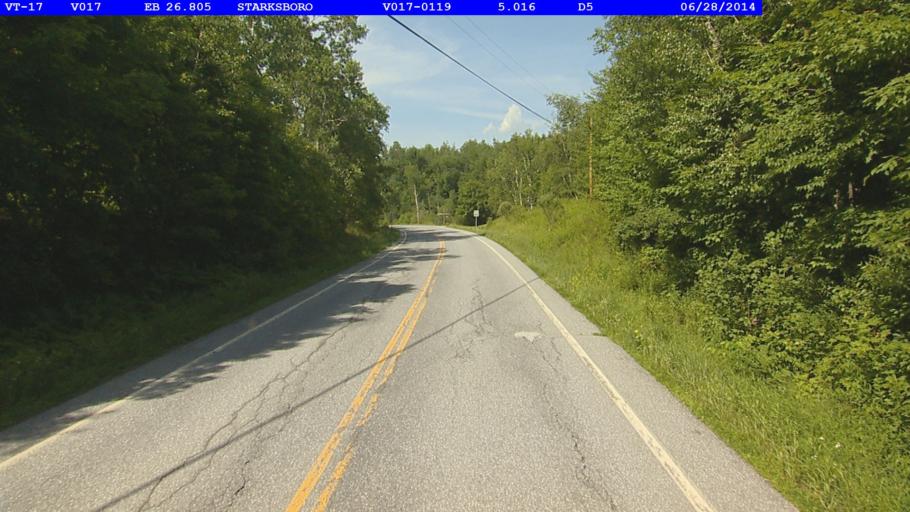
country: US
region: Vermont
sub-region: Addison County
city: Bristol
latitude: 44.2113
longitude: -72.9652
